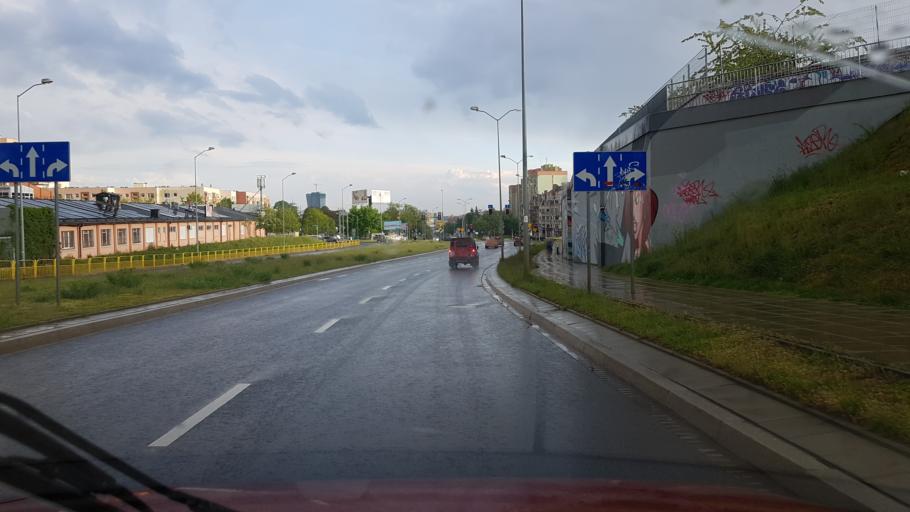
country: PL
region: West Pomeranian Voivodeship
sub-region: Szczecin
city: Szczecin
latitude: 53.4560
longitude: 14.5509
